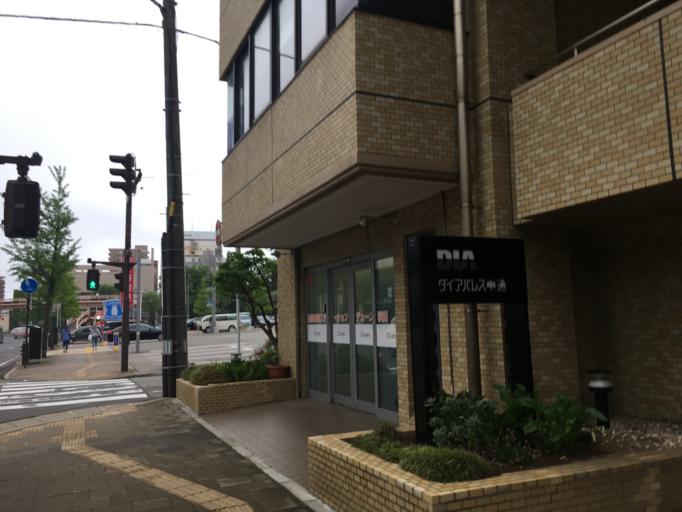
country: JP
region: Akita
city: Akita
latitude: 39.7165
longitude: 140.1197
